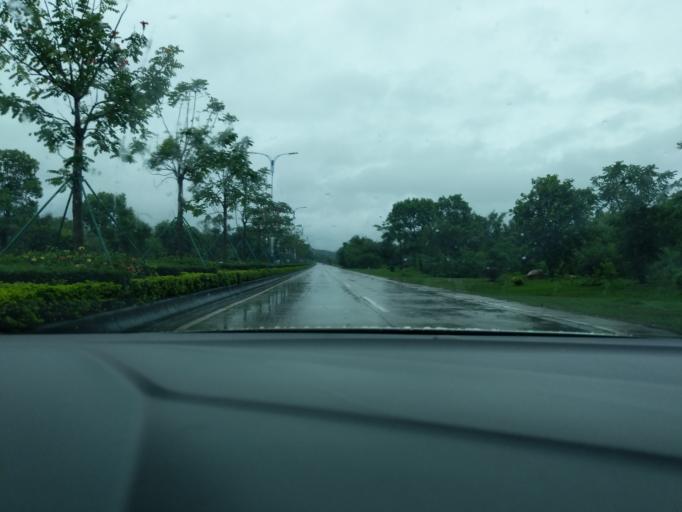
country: CN
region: Guangdong
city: Pingshi
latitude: 22.2186
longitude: 112.3173
